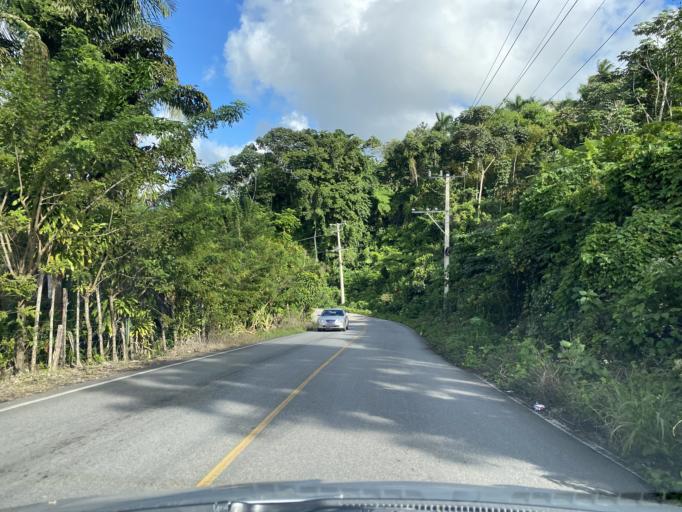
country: DO
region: Samana
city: Las Terrenas
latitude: 19.2744
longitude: -69.5508
